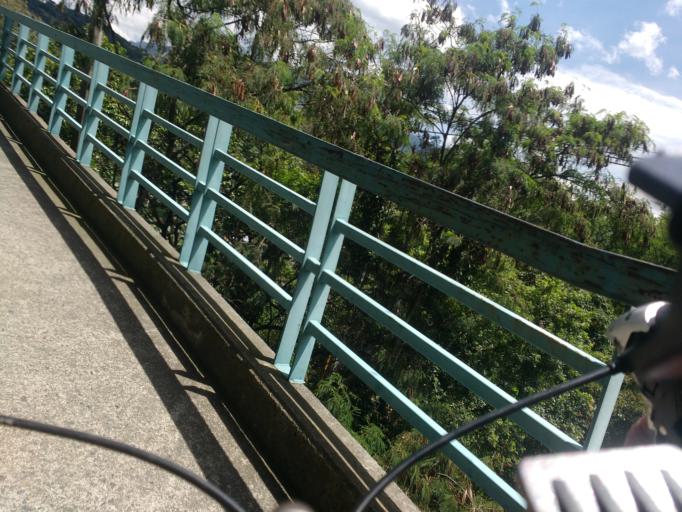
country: CO
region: Antioquia
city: Medellin
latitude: 6.2643
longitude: -75.5725
